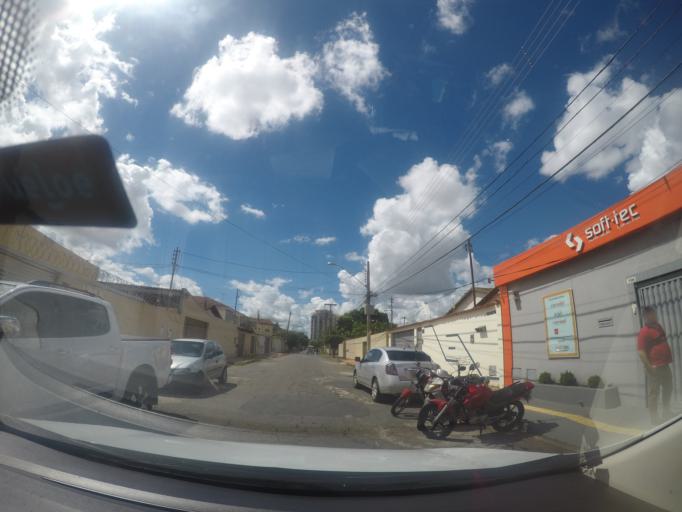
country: BR
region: Goias
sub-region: Goiania
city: Goiania
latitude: -16.6822
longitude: -49.2782
